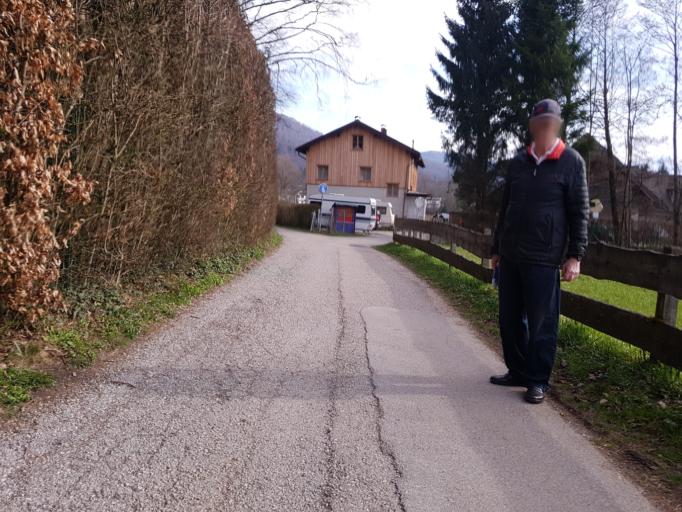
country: AT
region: Salzburg
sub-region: Politischer Bezirk Salzburg-Umgebung
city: Elsbethen
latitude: 47.7924
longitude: 13.0864
